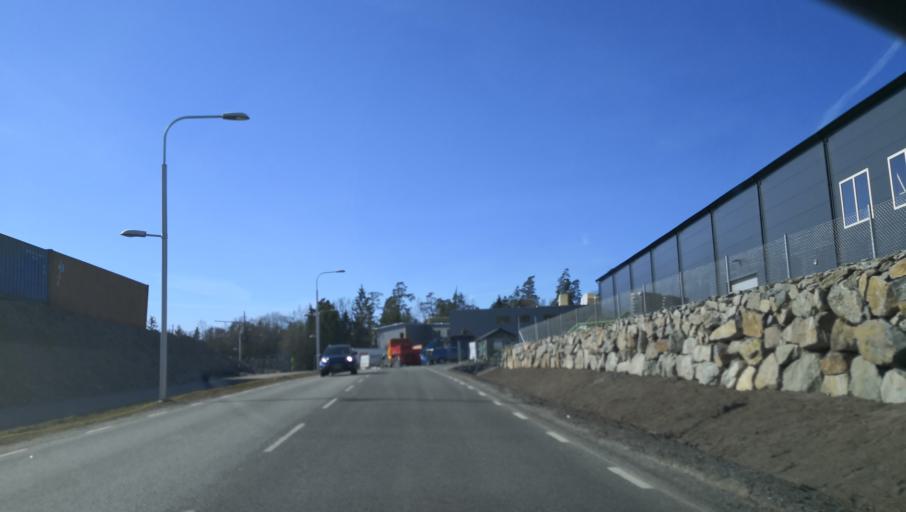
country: SE
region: Stockholm
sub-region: Varmdo Kommun
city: Gustavsberg
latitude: 59.3134
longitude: 18.3693
